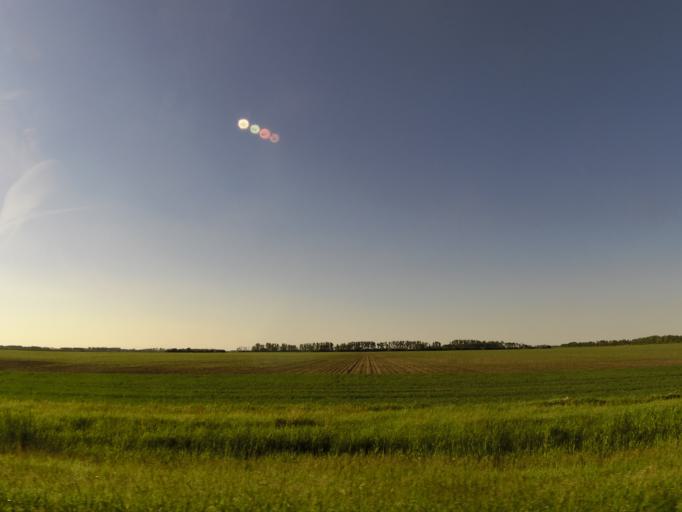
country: US
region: North Dakota
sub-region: Grand Forks County
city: Grand Forks Air Force Base
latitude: 48.1357
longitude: -97.2289
